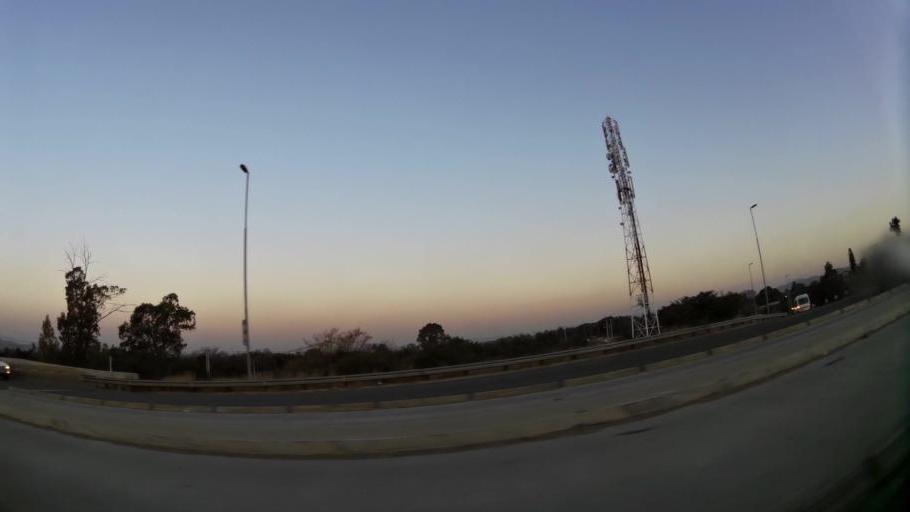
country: ZA
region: North-West
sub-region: Bojanala Platinum District Municipality
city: Rustenburg
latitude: -25.6467
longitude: 27.2565
